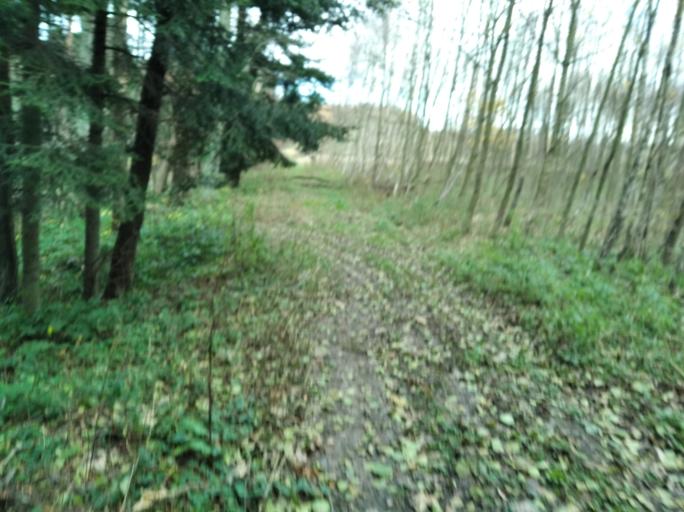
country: PL
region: Subcarpathian Voivodeship
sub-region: Powiat strzyzowski
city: Jawornik
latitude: 49.8654
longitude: 21.8560
